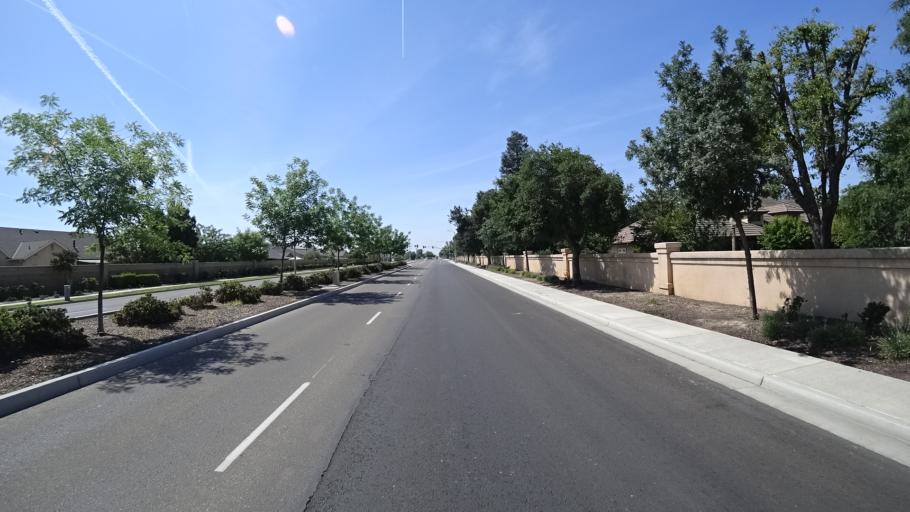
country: US
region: California
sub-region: Kings County
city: Lucerne
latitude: 36.3526
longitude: -119.6729
